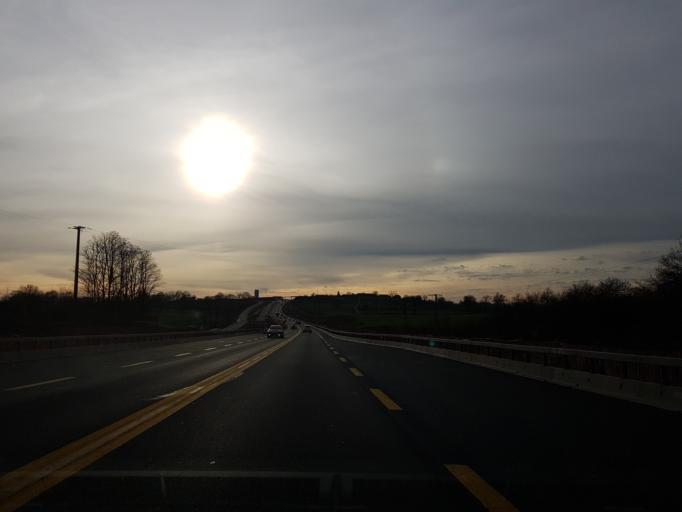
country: FR
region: Auvergne
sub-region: Departement de l'Allier
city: Montmarault
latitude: 46.3427
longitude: 2.9872
